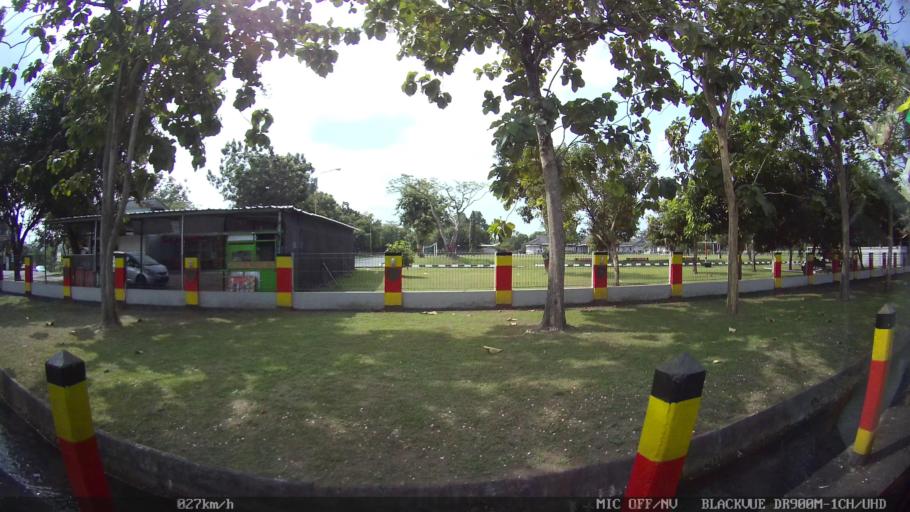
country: ID
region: Daerah Istimewa Yogyakarta
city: Depok
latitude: -7.8040
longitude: 110.4233
